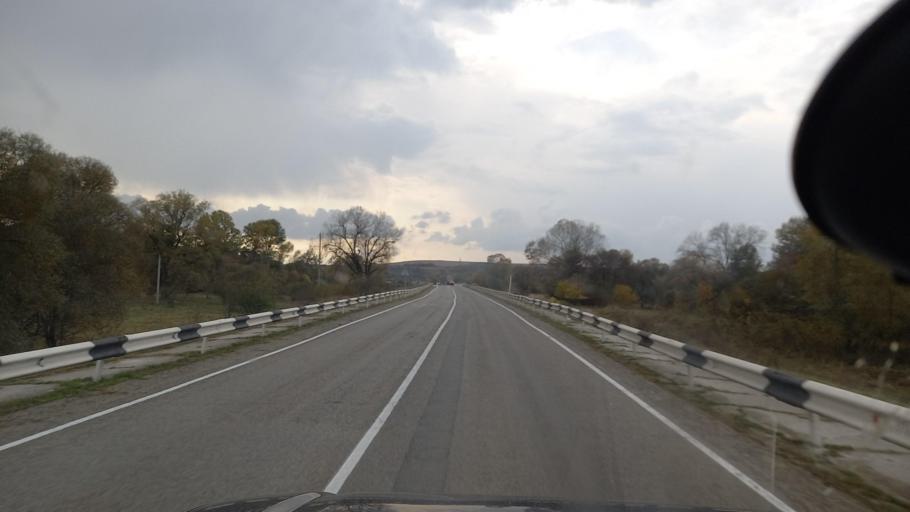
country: RU
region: Krasnodarskiy
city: Mostovskoy
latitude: 44.3916
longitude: 40.7489
